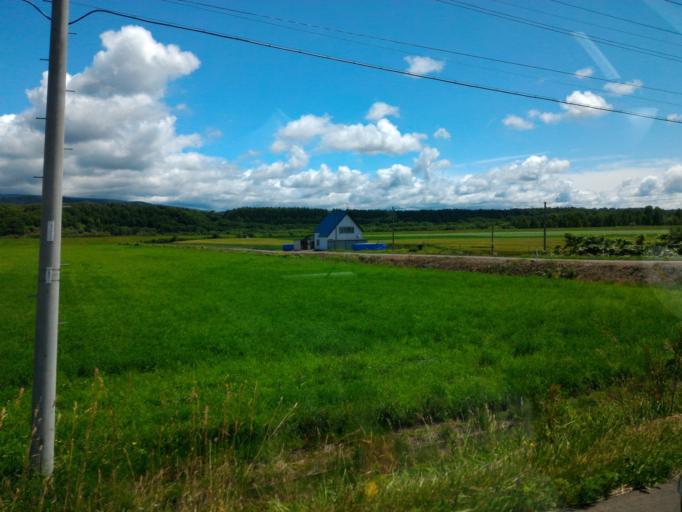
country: JP
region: Hokkaido
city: Nayoro
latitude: 44.5320
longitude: 142.3244
